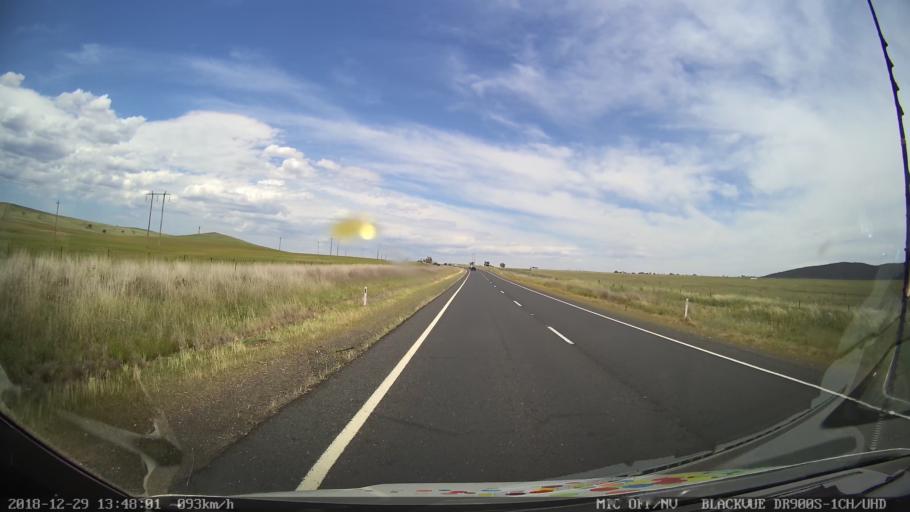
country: AU
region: New South Wales
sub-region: Cooma-Monaro
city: Cooma
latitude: -36.1346
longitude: 149.1455
